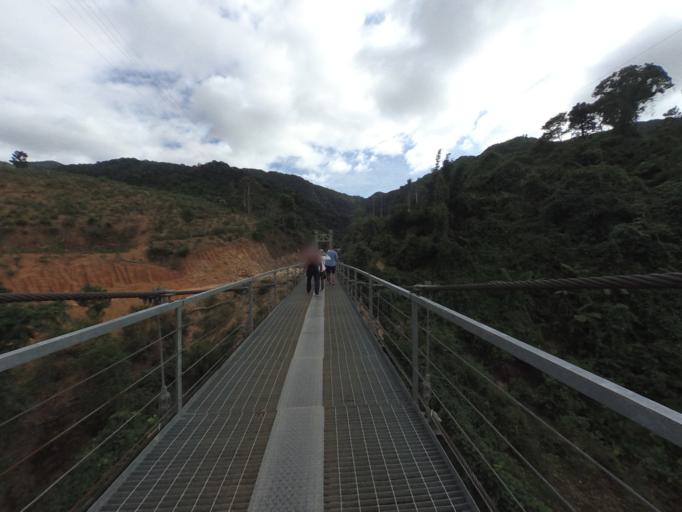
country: VN
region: Thua Thien-Hue
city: A Luoi
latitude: 16.3045
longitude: 107.2138
